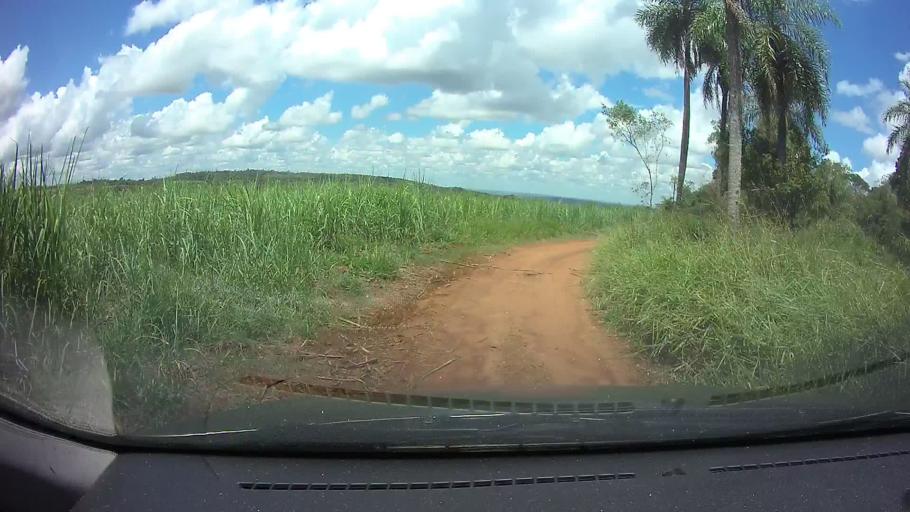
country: PY
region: Paraguari
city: La Colmena
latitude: -25.9694
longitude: -56.7329
